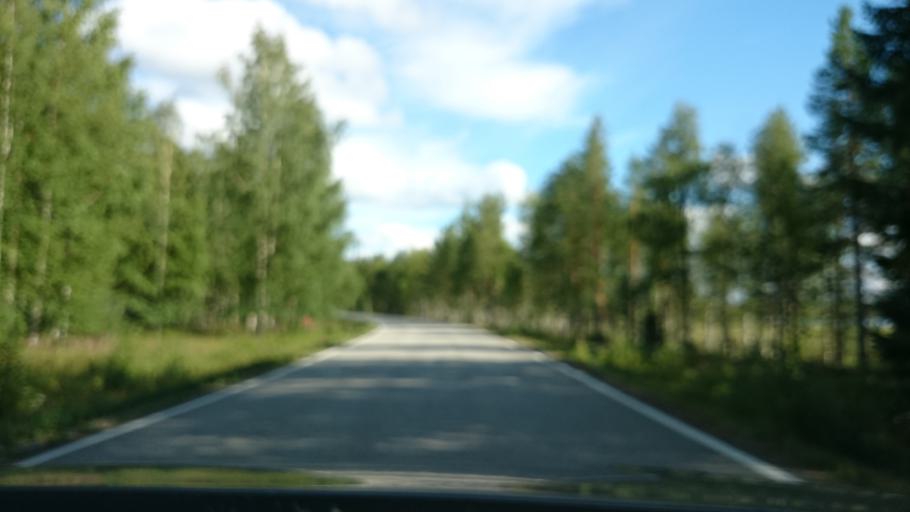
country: FI
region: Kainuu
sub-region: Kehys-Kainuu
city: Suomussalmi
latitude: 64.7580
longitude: 29.3909
